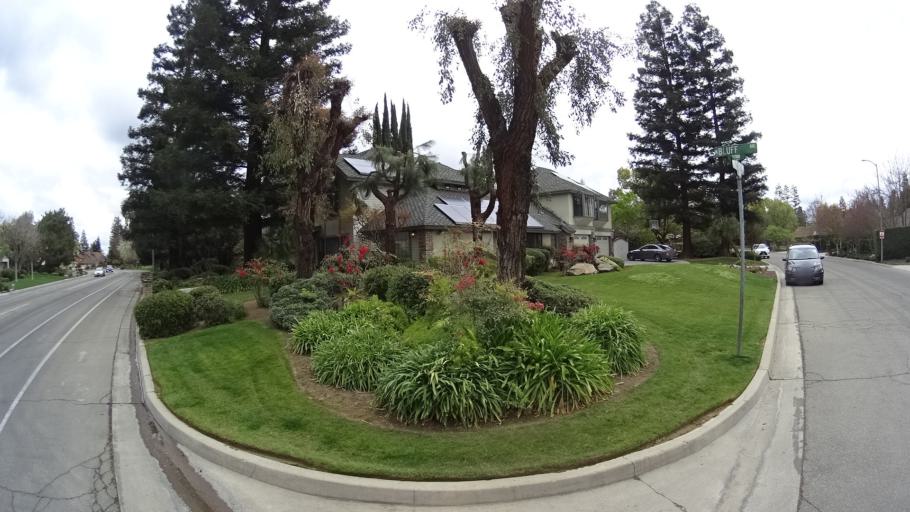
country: US
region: California
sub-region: Fresno County
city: Fresno
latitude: 36.8489
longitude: -119.8437
